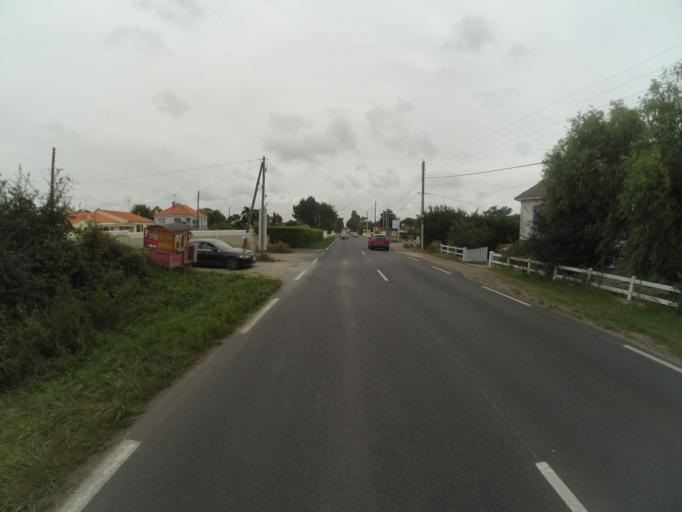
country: FR
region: Pays de la Loire
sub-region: Departement de la Vendee
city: Challans
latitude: 46.8608
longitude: -1.9109
